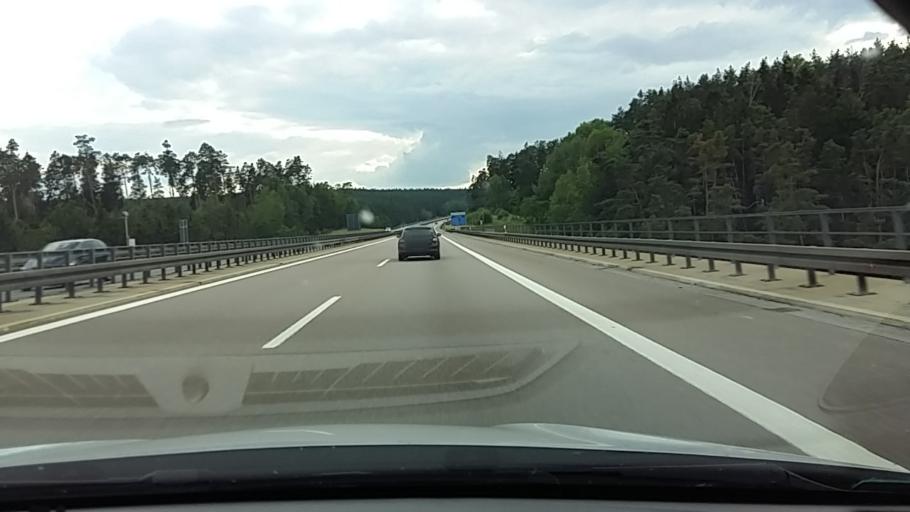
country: DE
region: Bavaria
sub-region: Upper Palatinate
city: Kummersbruck
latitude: 49.3946
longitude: 11.9046
